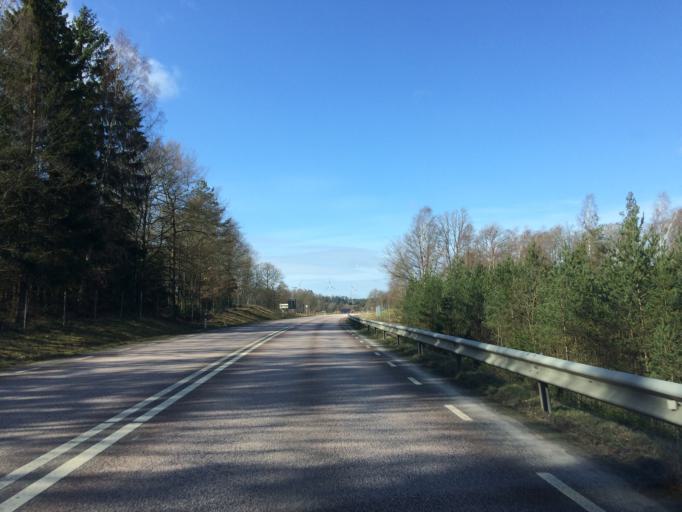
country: SE
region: Halland
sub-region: Laholms Kommun
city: Knared
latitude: 56.5239
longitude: 13.2503
